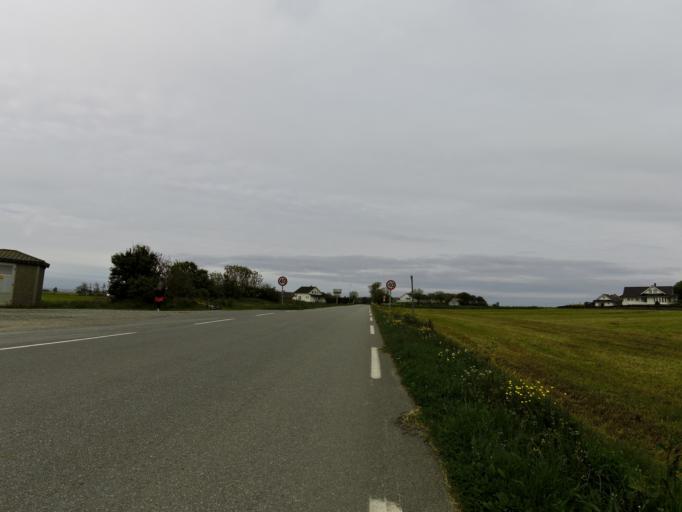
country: NO
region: Rogaland
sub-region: Klepp
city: Kleppe
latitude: 58.8171
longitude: 5.5711
